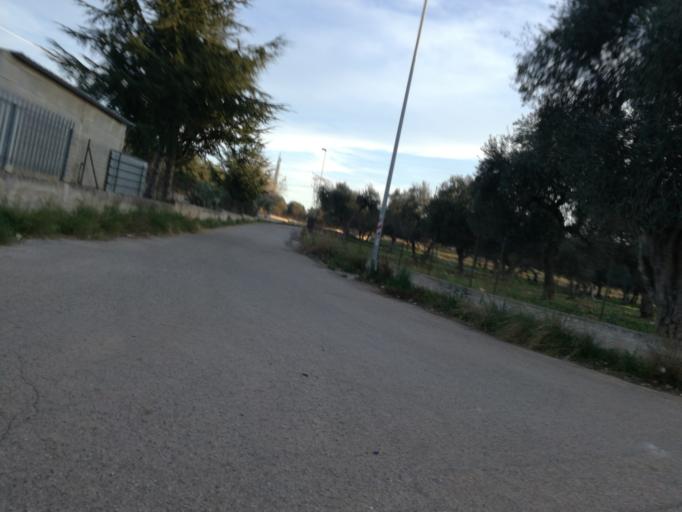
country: IT
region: Apulia
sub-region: Provincia di Bari
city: Lamie
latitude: 41.0318
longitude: 16.8780
